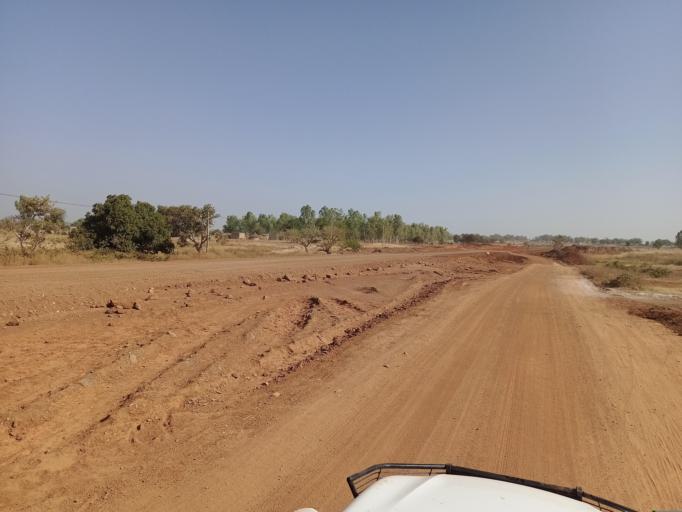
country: BF
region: Centre-Est
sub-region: Province du Boulgou
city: Tenkodogo
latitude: 11.5309
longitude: -0.4855
